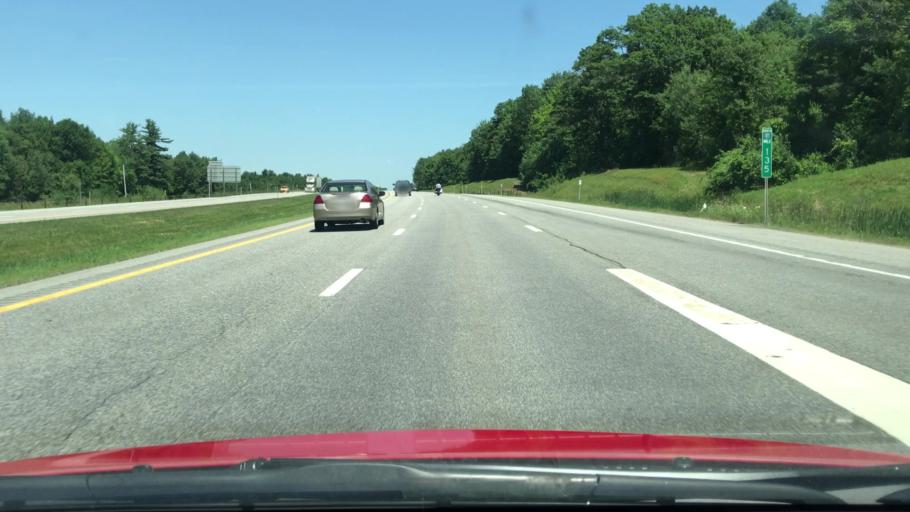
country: US
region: New York
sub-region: Essex County
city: Keeseville
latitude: 44.4472
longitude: -73.4897
